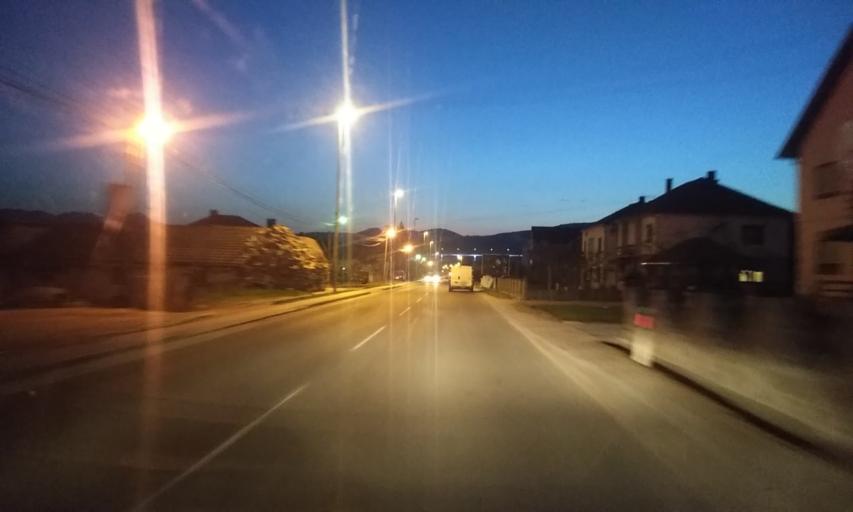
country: RS
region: Central Serbia
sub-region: Pcinjski Okrug
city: Vladicin Han
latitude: 42.7107
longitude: 22.0952
